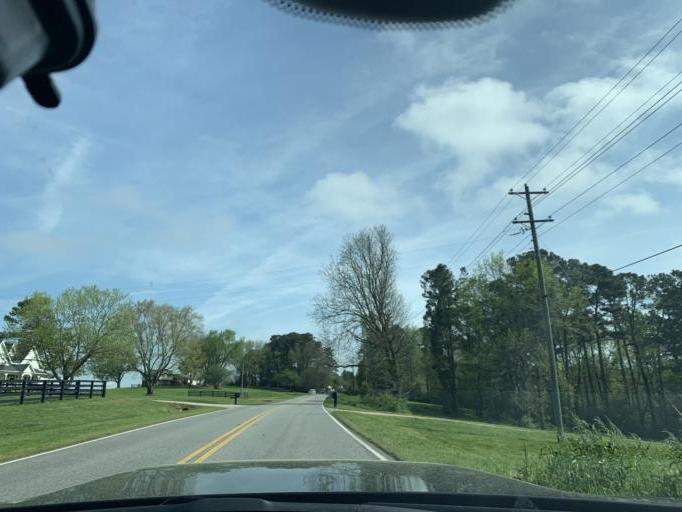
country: US
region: Georgia
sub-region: Forsyth County
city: Cumming
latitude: 34.2450
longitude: -84.0834
